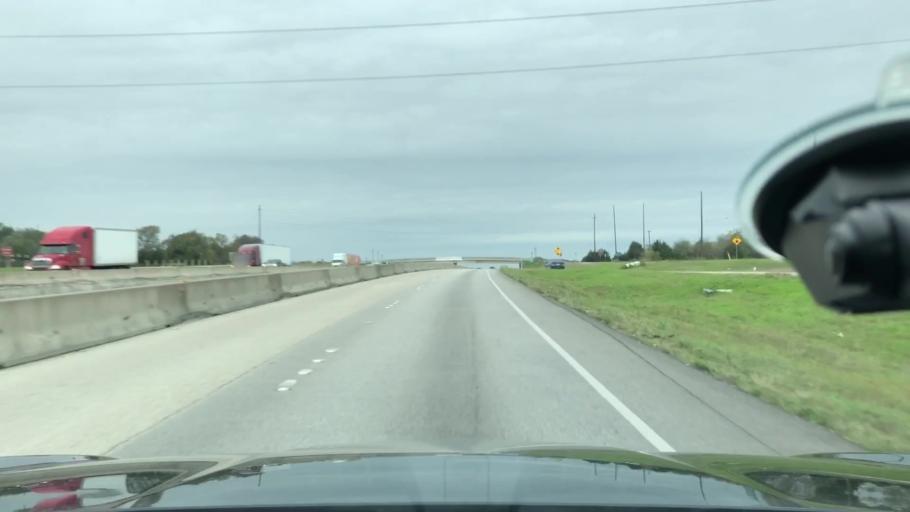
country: US
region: Texas
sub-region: Ellis County
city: Waxahachie
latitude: 32.3759
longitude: -96.8642
